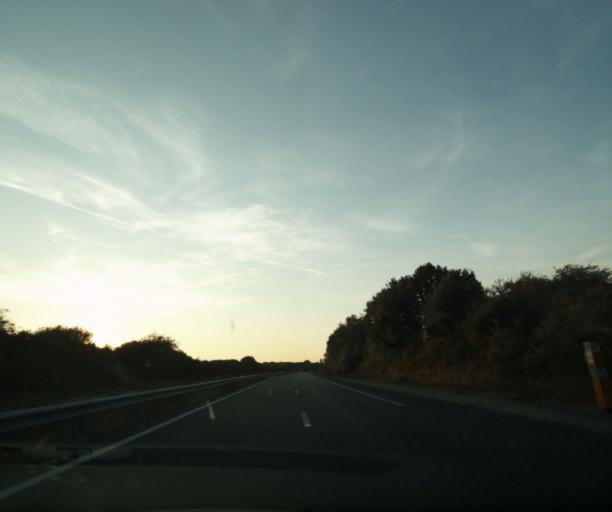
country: FR
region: Aquitaine
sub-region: Departement du Lot-et-Garonne
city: Fourques-sur-Garonne
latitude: 44.3807
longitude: 0.2111
